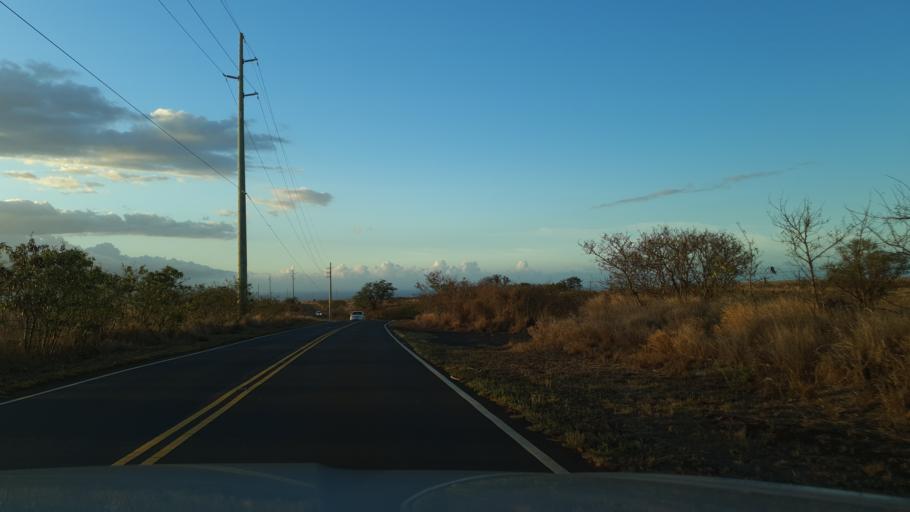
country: US
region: Hawaii
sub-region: Maui County
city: Pukalani
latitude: 20.8117
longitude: -156.3827
